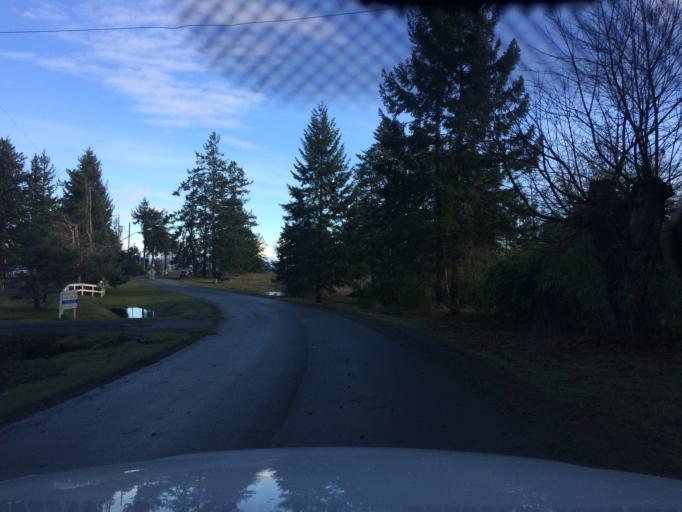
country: CA
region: British Columbia
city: Campbell River
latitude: 49.8880
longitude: -125.1288
